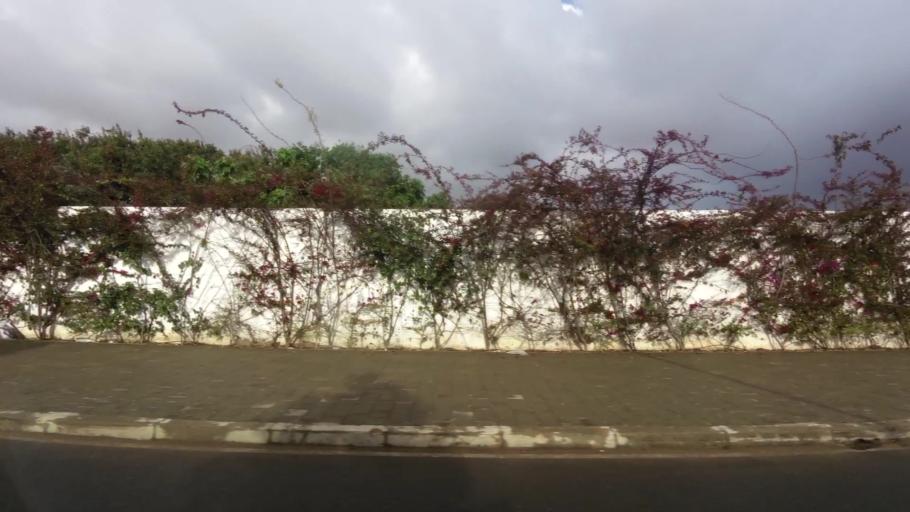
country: MA
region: Grand Casablanca
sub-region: Casablanca
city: Casablanca
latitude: 33.5524
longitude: -7.6515
